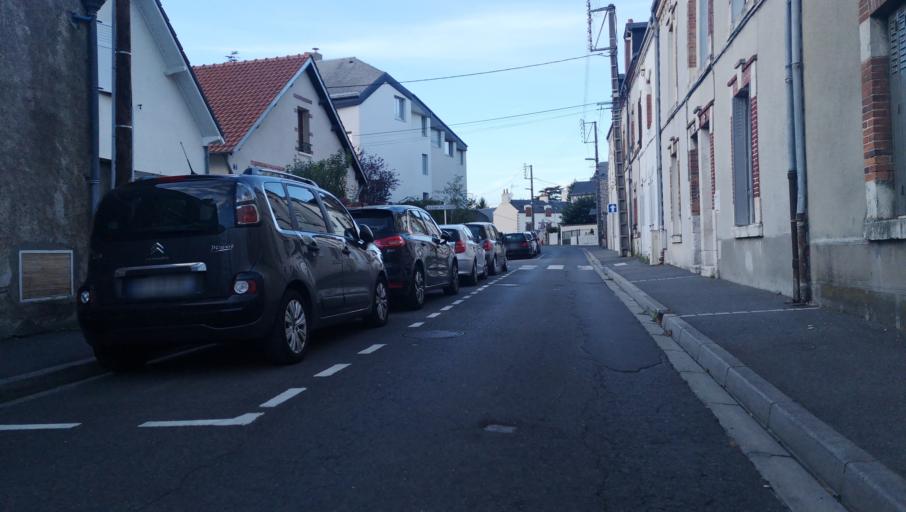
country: FR
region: Centre
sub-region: Departement du Loiret
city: Orleans
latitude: 47.9027
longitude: 1.8862
